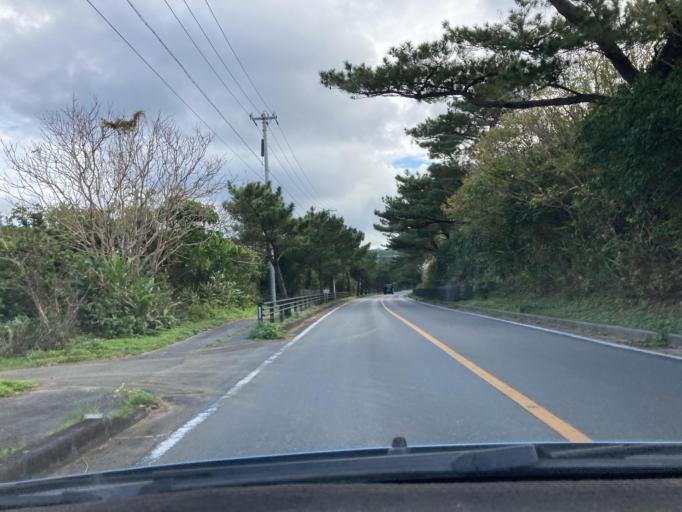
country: JP
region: Okinawa
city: Nago
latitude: 26.8630
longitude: 128.2599
